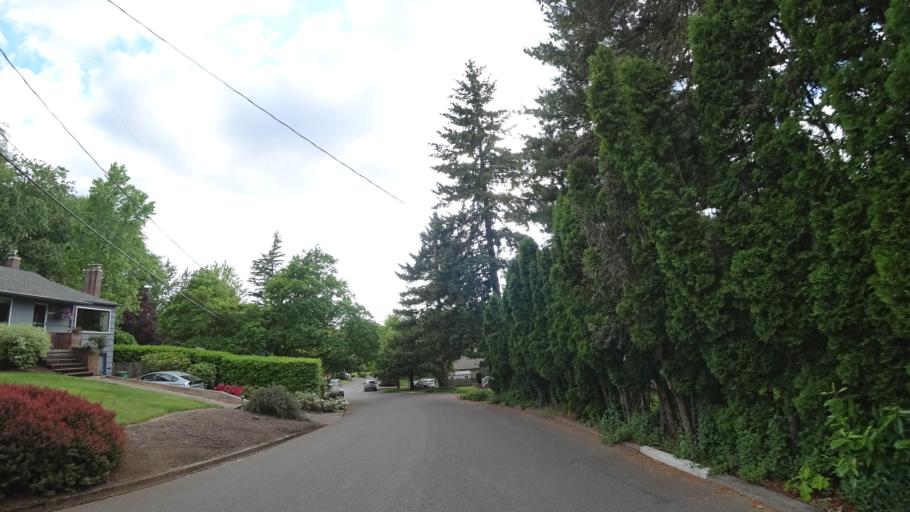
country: US
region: Oregon
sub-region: Washington County
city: Garden Home-Whitford
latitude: 45.4775
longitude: -122.7290
